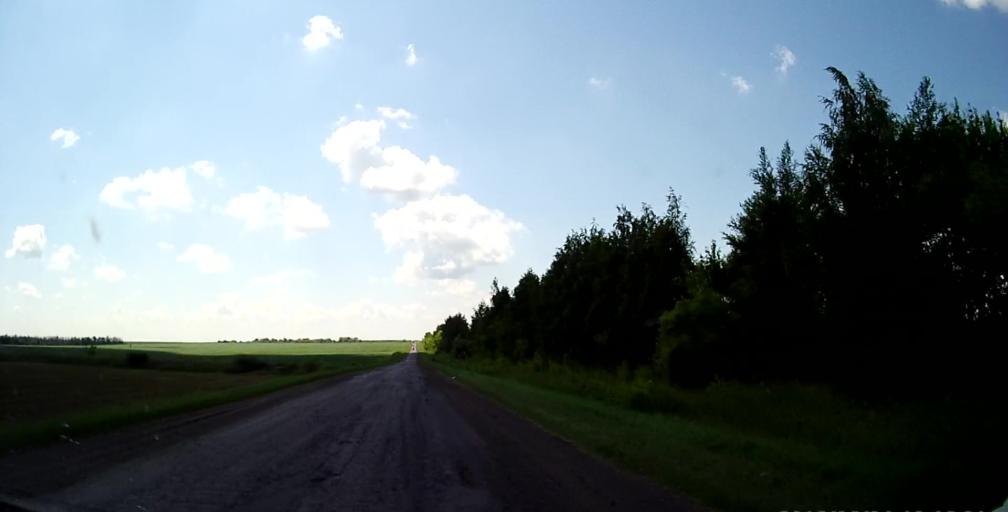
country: RU
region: Lipetsk
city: Chaplygin
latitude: 53.2854
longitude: 39.9596
